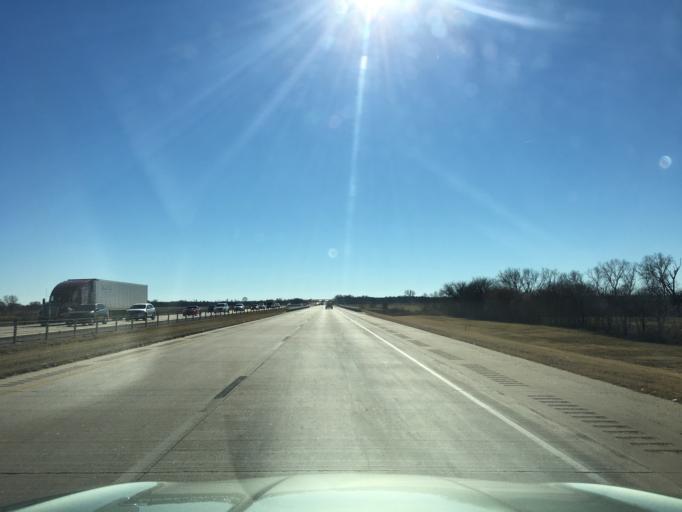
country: US
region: Oklahoma
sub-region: Noble County
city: Perry
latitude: 36.4731
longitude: -97.3272
